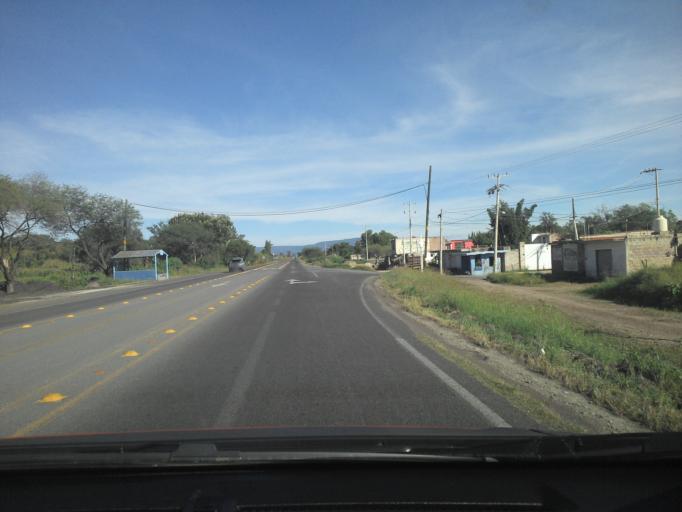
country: MX
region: Jalisco
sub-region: Teuchitlan
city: La Estanzuela
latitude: 20.6736
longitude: -103.8265
